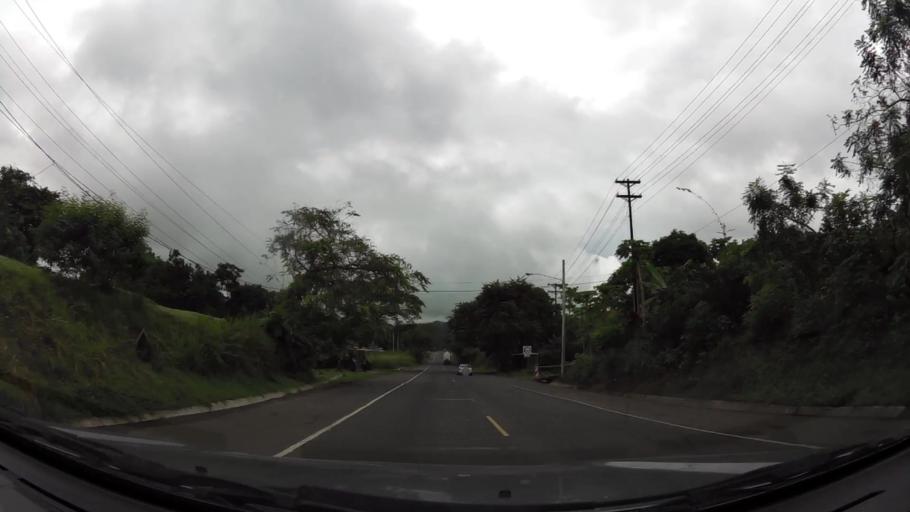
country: PA
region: Colon
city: Nuevo Vigia
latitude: 9.1989
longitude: -79.6237
